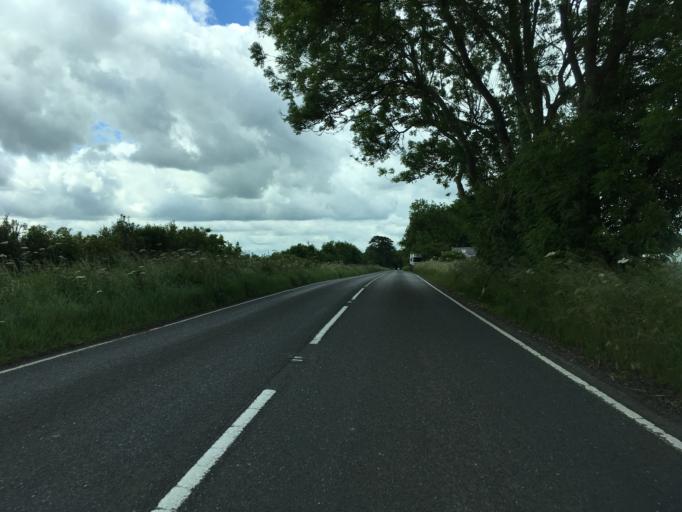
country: GB
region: England
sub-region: Oxfordshire
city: Shipton under Wychwood
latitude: 51.8946
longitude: -1.5629
